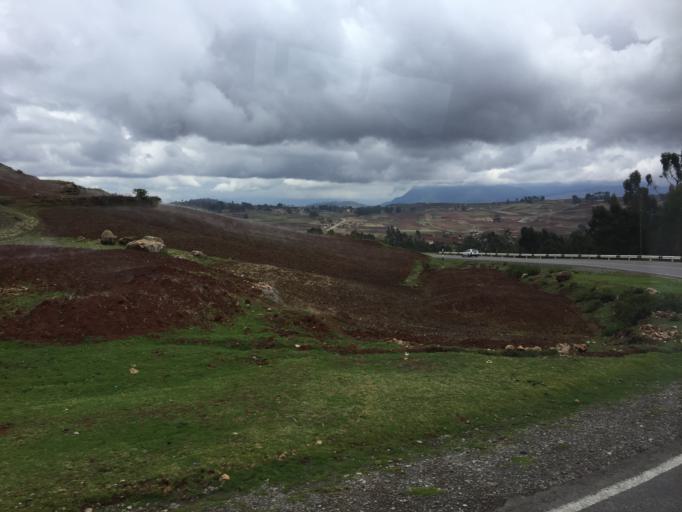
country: PE
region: Cusco
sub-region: Provincia de Urubamba
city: Huayllabamba
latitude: -13.3645
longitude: -72.0676
